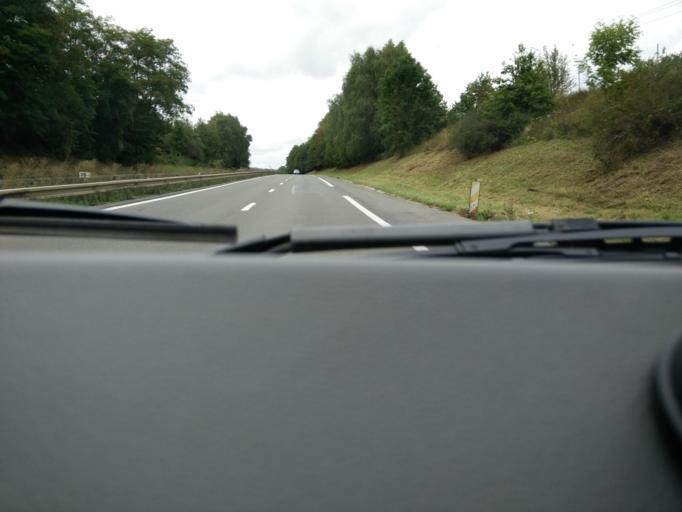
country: FR
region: Champagne-Ardenne
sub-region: Departement des Ardennes
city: Donchery
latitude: 49.7164
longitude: 4.8769
